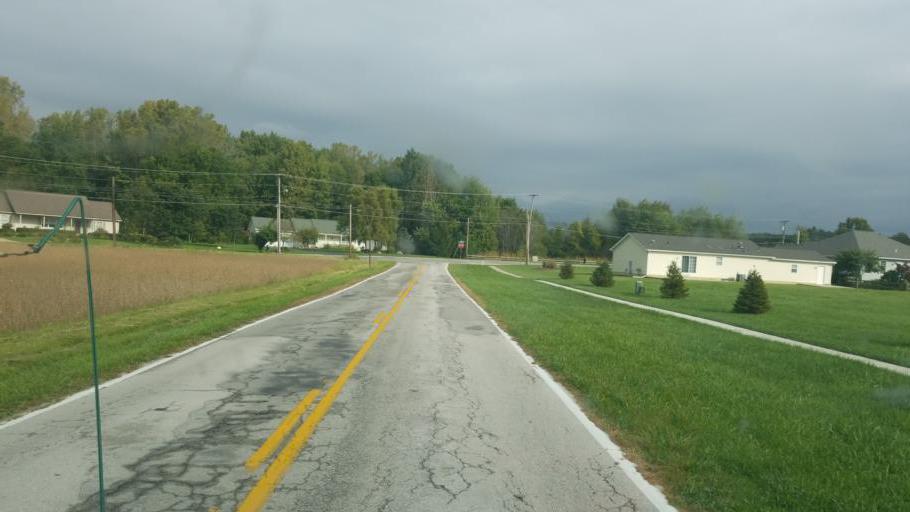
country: US
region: Ohio
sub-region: Wood County
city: Bowling Green
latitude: 41.3582
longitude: -83.6699
